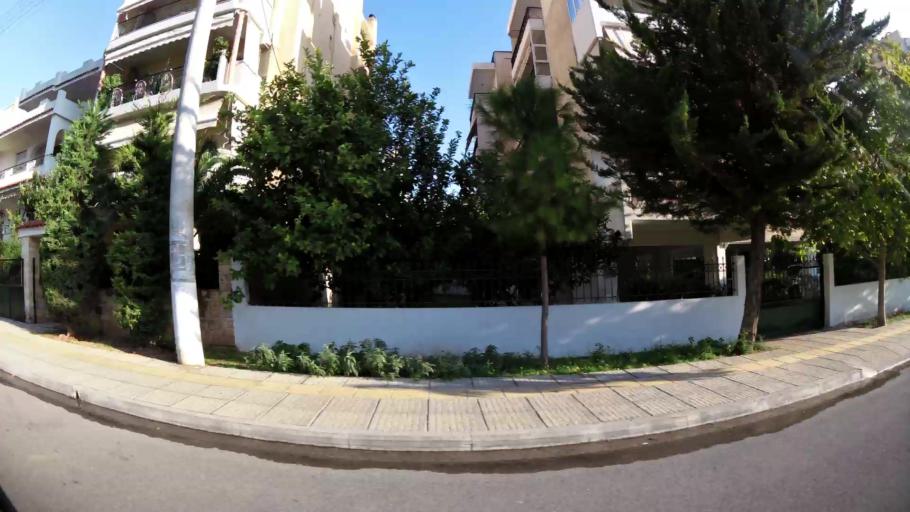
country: GR
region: Attica
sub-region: Nomarchia Athinas
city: Argyroupoli
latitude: 37.8998
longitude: 23.7648
